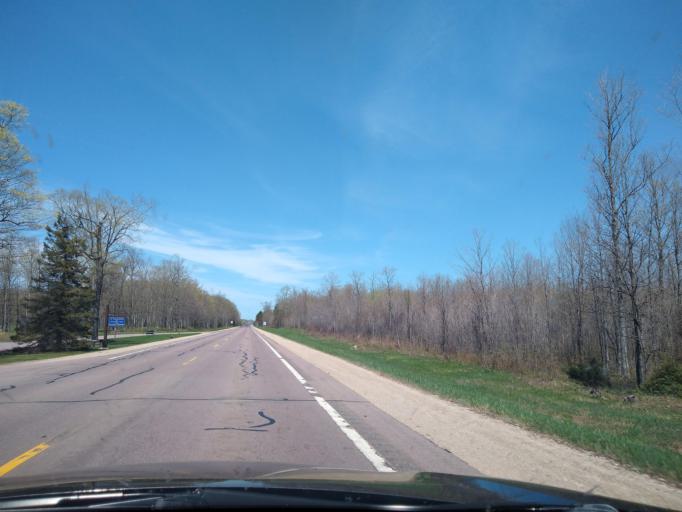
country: US
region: Michigan
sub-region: Marquette County
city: K. I. Sawyer Air Force Base
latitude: 46.2397
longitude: -87.0759
